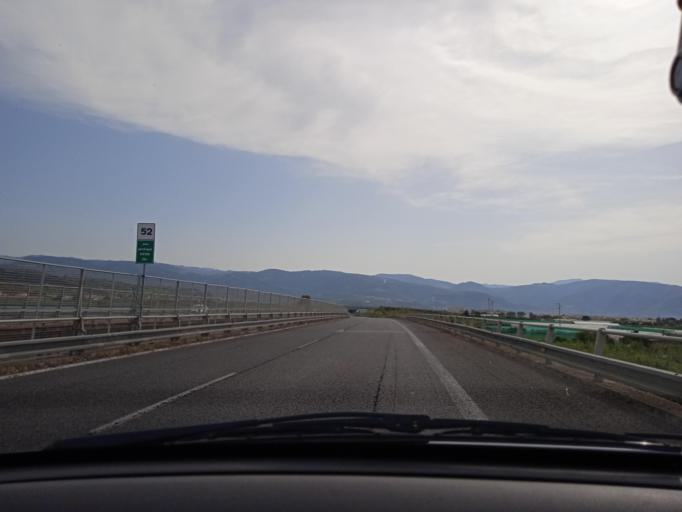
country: IT
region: Sicily
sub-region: Messina
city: Vigliatore 2
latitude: 38.1324
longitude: 15.1354
